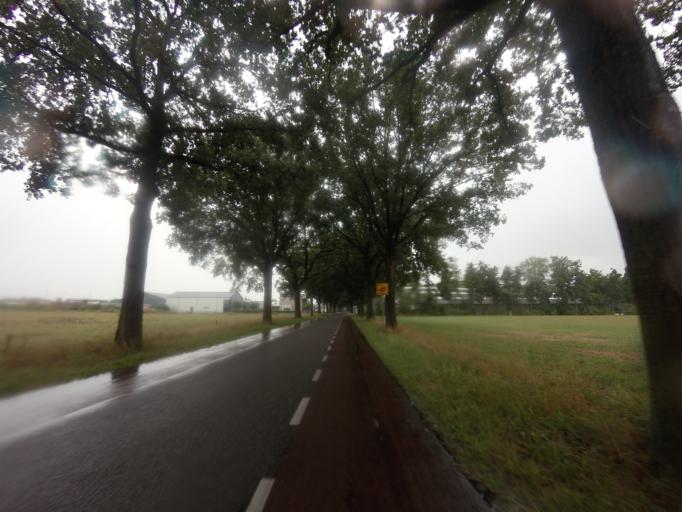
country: NL
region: Drenthe
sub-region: Gemeente Hoogeveen
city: Hoogeveen
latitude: 52.6079
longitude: 6.3948
